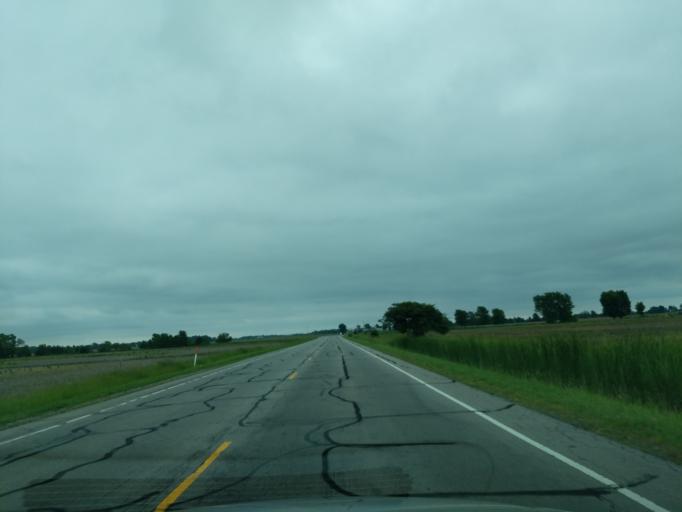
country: US
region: Indiana
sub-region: Madison County
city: Alexandria
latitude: 40.2772
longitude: -85.5804
